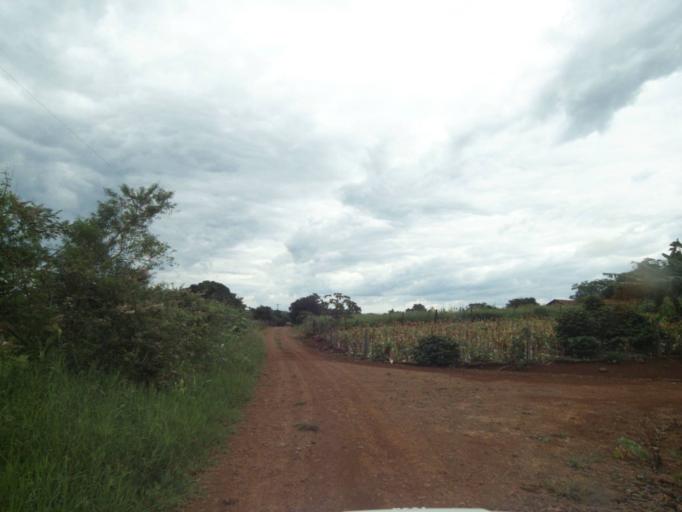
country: BR
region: Parana
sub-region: Guaraniacu
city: Guaraniacu
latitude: -24.9164
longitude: -52.9358
